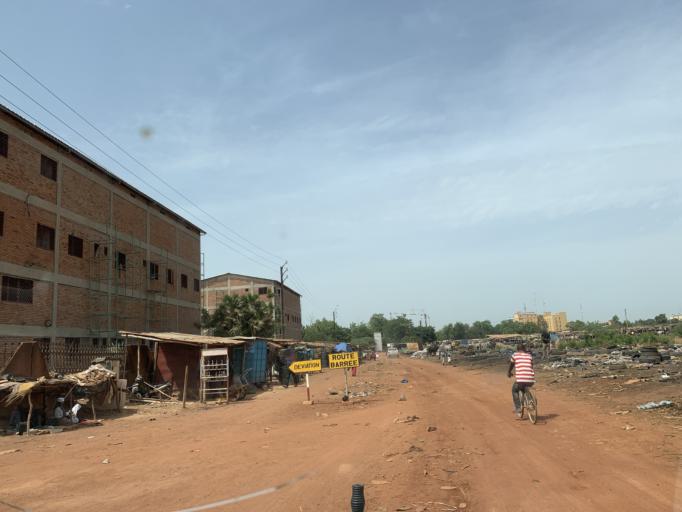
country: BF
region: Centre
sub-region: Kadiogo Province
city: Ouagadougou
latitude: 12.3373
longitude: -1.5150
